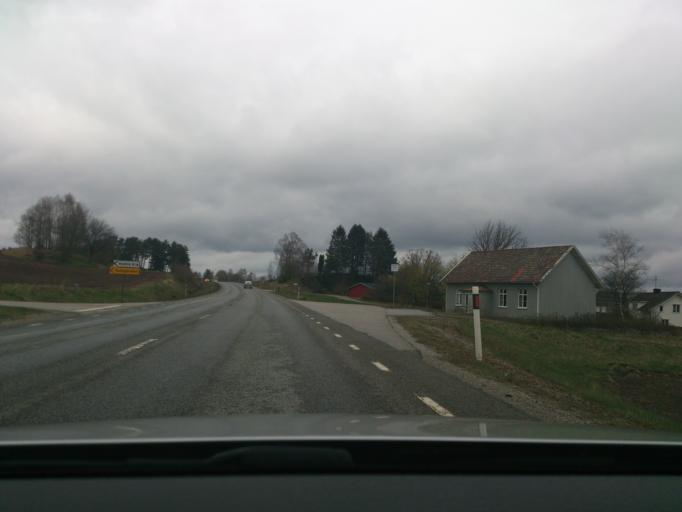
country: SE
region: Vaestra Goetaland
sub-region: Ulricehamns Kommun
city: Ulricehamn
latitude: 57.9574
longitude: 13.5222
